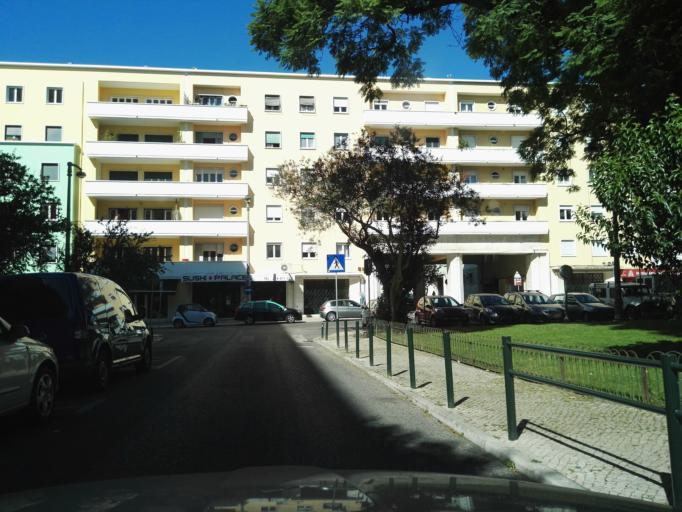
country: PT
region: Lisbon
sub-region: Lisbon
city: Lisbon
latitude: 38.7409
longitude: -9.1358
